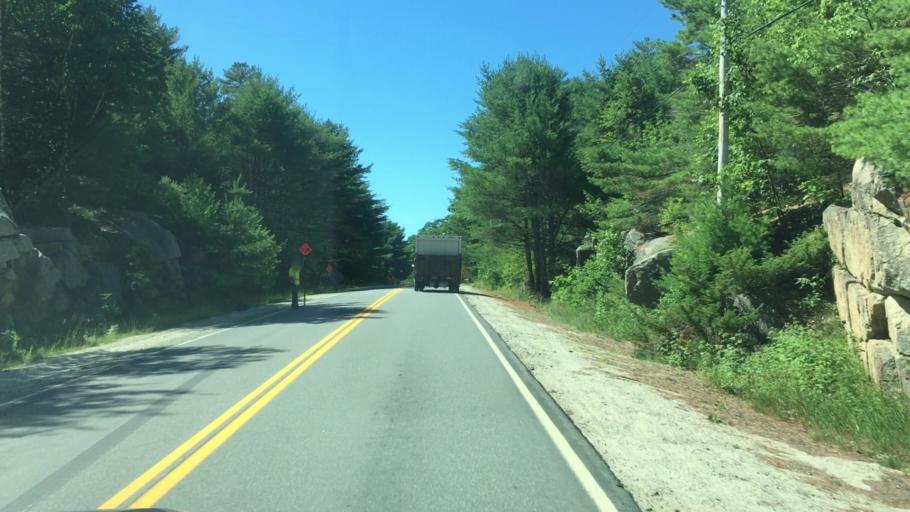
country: US
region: Maine
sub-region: Hancock County
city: Sedgwick
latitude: 44.3501
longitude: -68.5873
